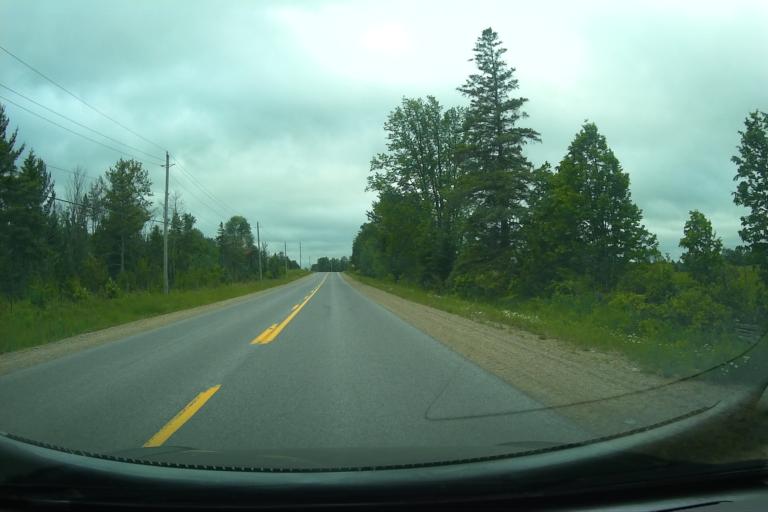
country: CA
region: Ontario
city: Pembroke
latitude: 45.4966
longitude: -77.1557
